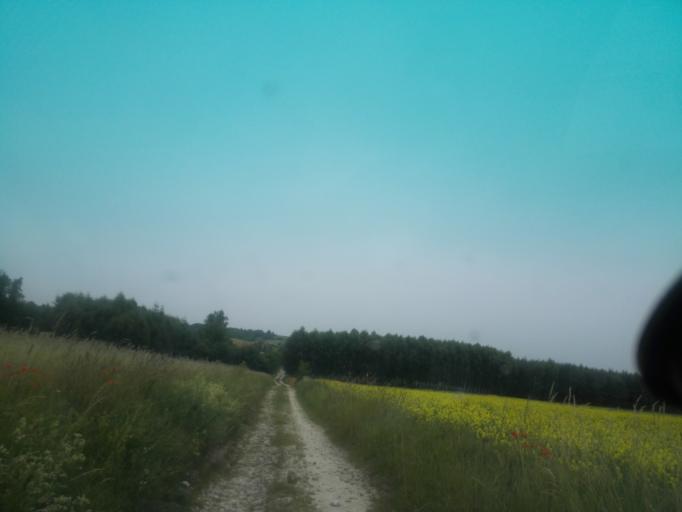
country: PL
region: Silesian Voivodeship
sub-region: Powiat czestochowski
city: Mstow
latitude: 50.7923
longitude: 19.3621
